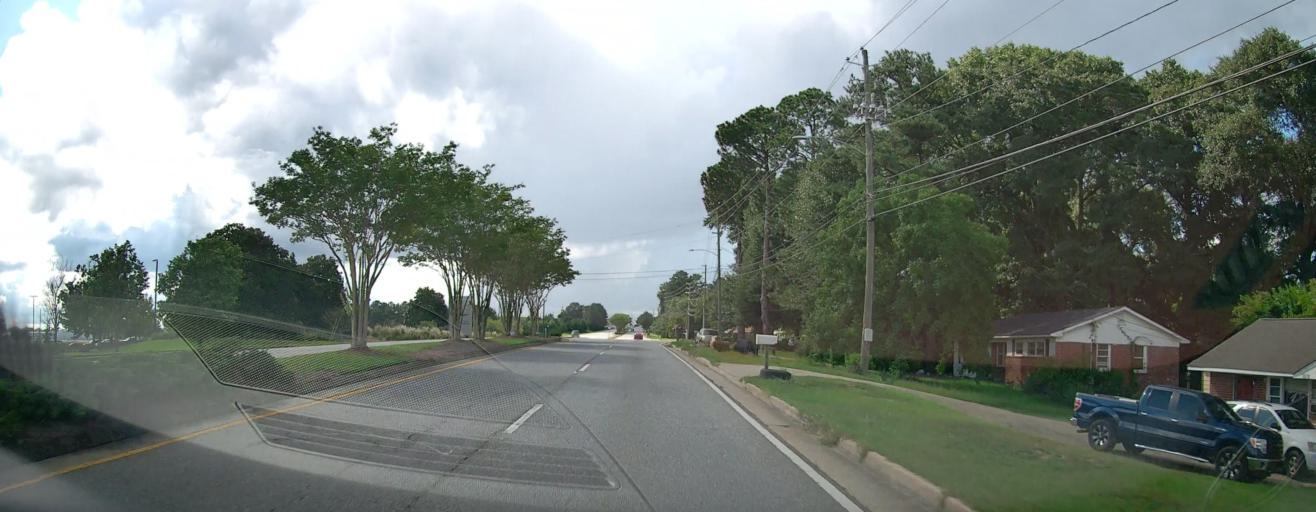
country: US
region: Georgia
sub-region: Muscogee County
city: Columbus
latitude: 32.5195
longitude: -84.9387
